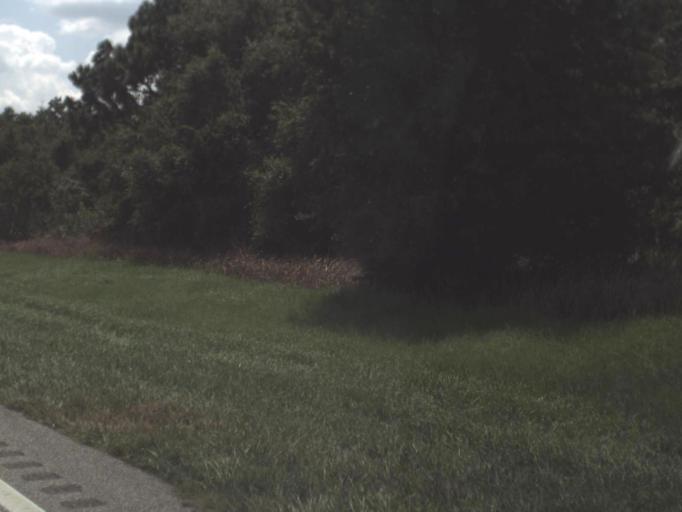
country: US
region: Florida
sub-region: Hillsborough County
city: Sun City Center
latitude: 27.6840
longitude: -82.3453
